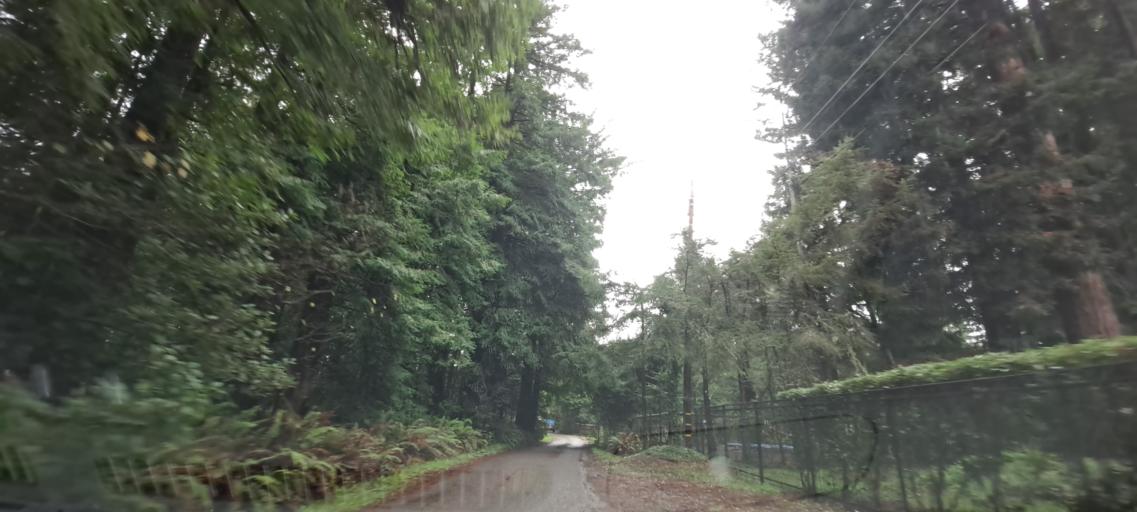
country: US
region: California
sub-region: Humboldt County
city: Fortuna
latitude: 40.6058
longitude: -124.1391
